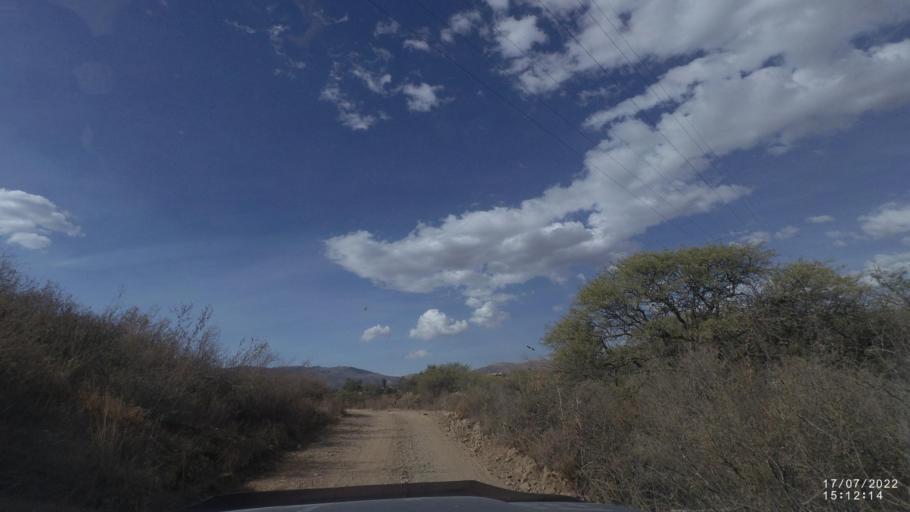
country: BO
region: Cochabamba
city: Capinota
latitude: -17.5708
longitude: -66.2641
